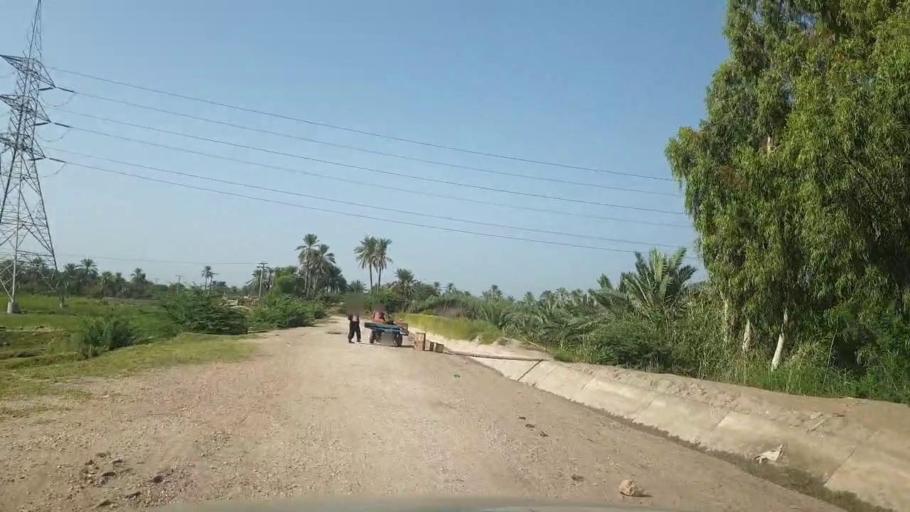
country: PK
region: Sindh
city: Rohri
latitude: 27.6623
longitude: 68.8839
